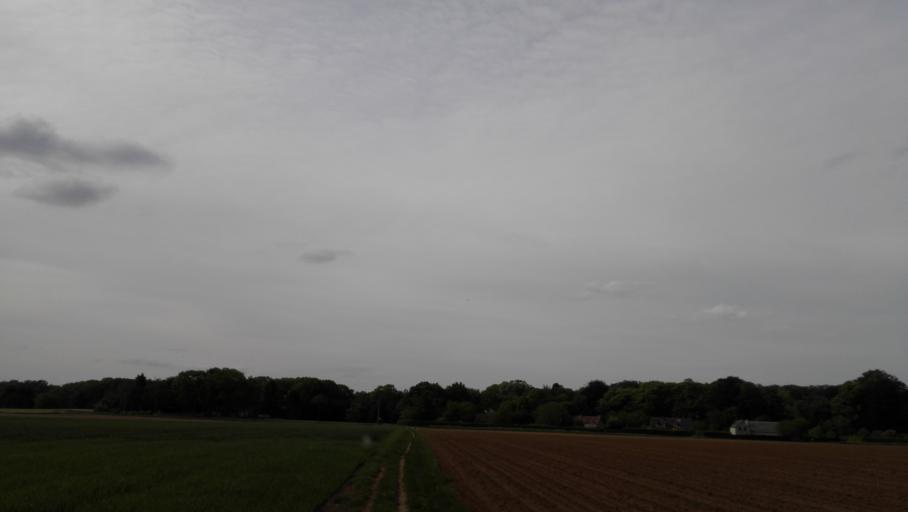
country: BE
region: Flanders
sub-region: Provincie Vlaams-Brabant
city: Holsbeek
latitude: 50.9091
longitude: 4.7583
